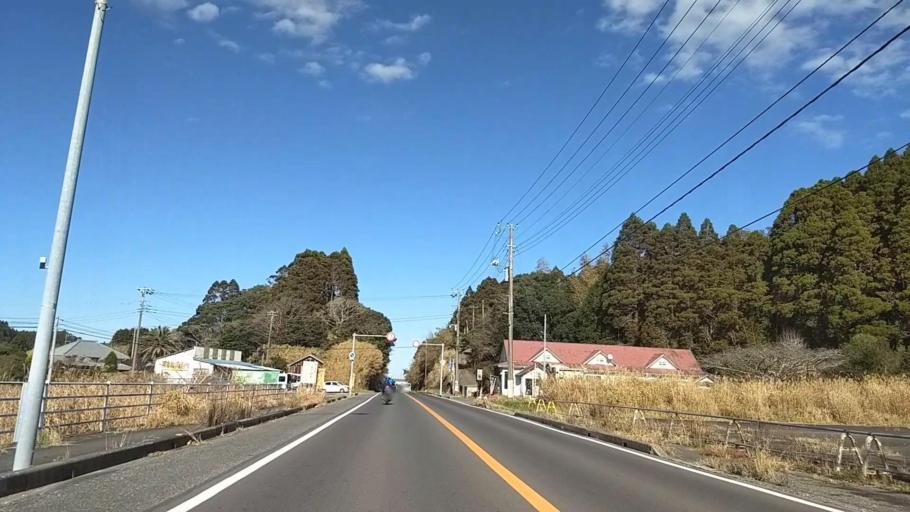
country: JP
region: Chiba
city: Ohara
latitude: 35.2144
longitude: 140.3769
